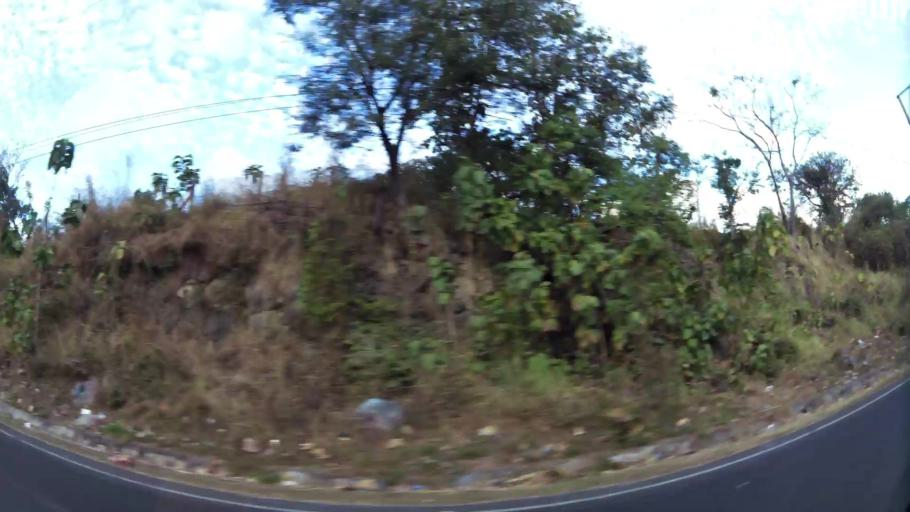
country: SV
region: San Vicente
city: Apastepeque
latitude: 13.6639
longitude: -88.7944
